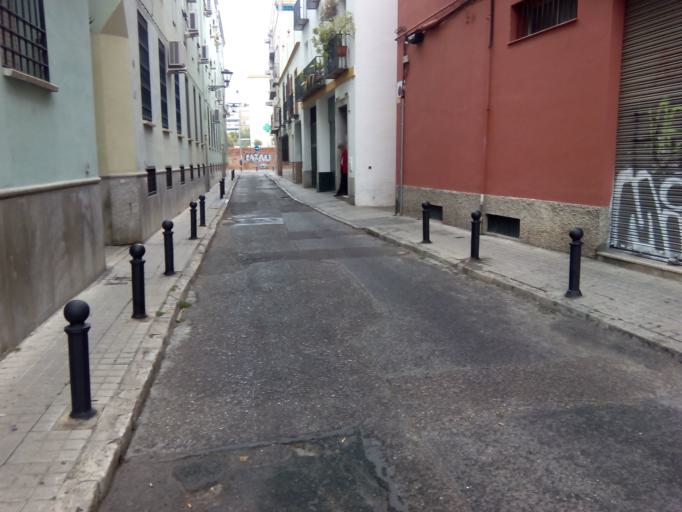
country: ES
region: Andalusia
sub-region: Provincia de Sevilla
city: Sevilla
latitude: 37.3977
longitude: -5.9838
